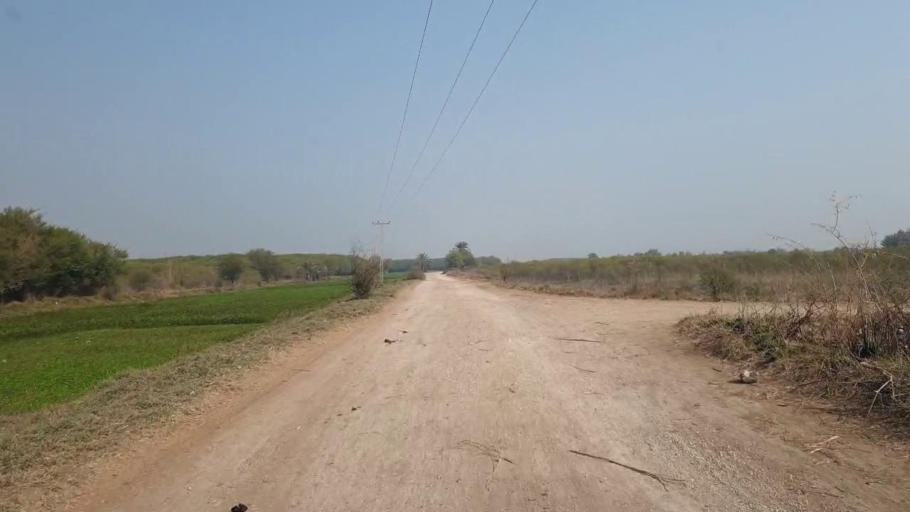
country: PK
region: Sindh
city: Hala
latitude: 25.9664
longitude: 68.4245
